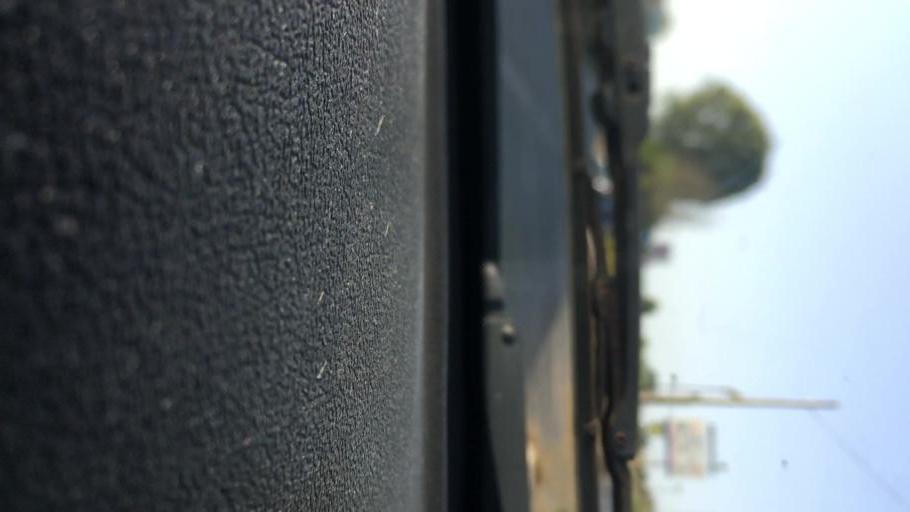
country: IT
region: Latium
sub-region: Citta metropolitana di Roma Capitale
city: Borgo Lotti
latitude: 41.8058
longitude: 12.5339
